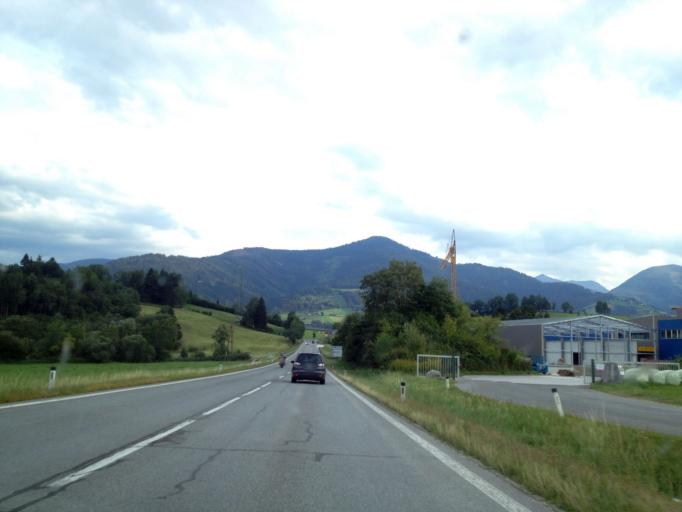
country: AT
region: Styria
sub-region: Politischer Bezirk Liezen
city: Grobming
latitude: 47.4508
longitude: 13.9122
